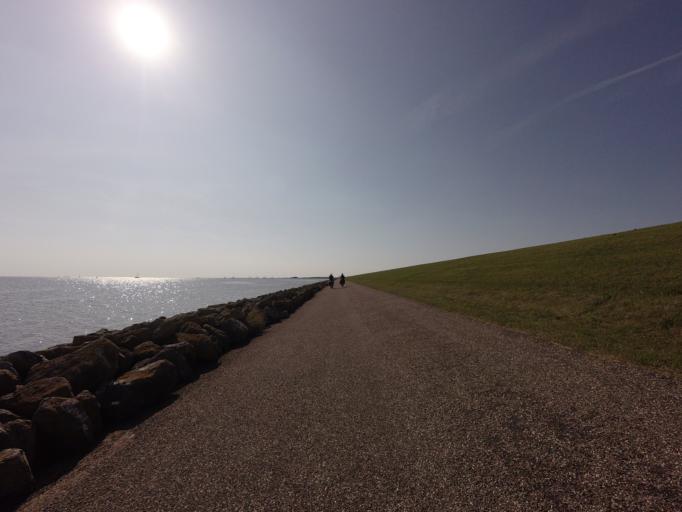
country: NL
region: Friesland
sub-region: Gemeente Schiermonnikoog
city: Schiermonnikoog
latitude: 53.4724
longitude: 6.1870
